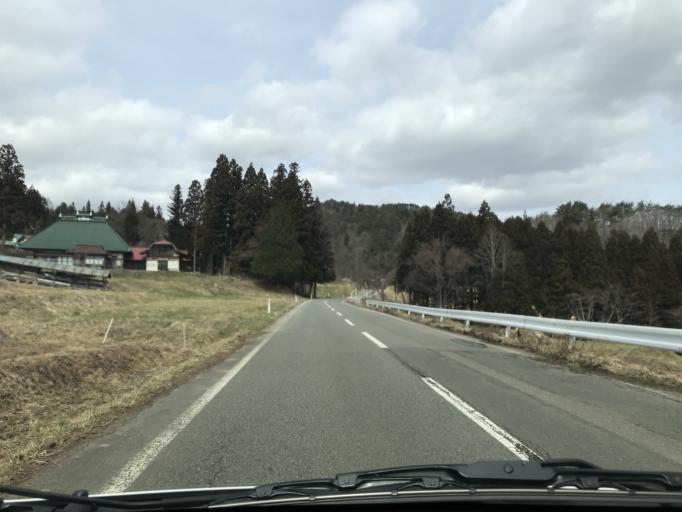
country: JP
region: Iwate
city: Kitakami
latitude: 39.2798
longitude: 141.3198
